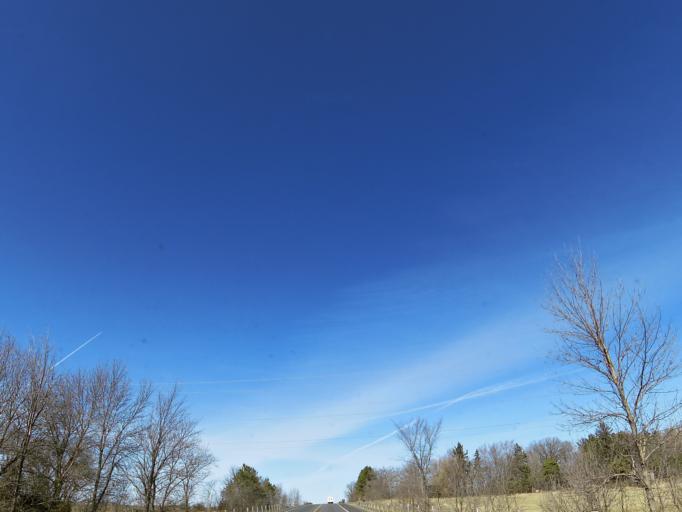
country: US
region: Minnesota
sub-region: Wright County
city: Rockford
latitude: 45.1113
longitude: -93.7846
